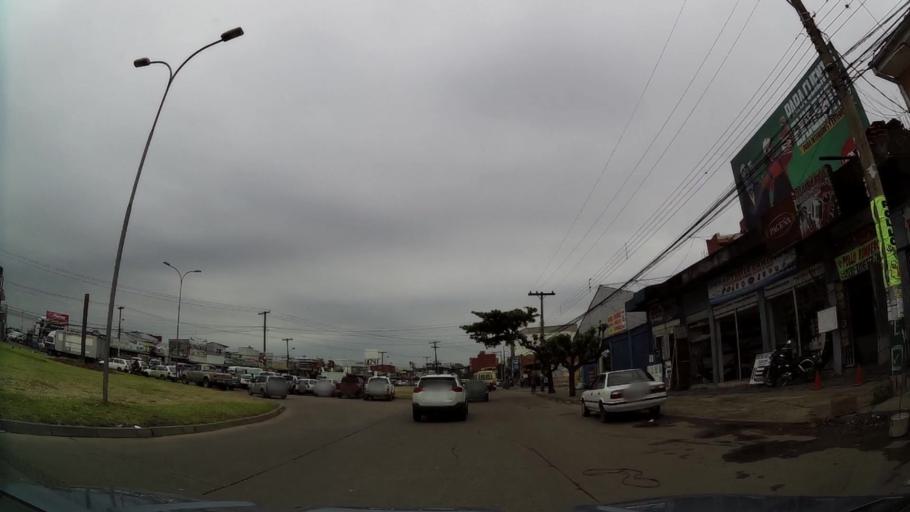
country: BO
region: Santa Cruz
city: Santa Cruz de la Sierra
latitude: -17.7845
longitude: -63.1578
